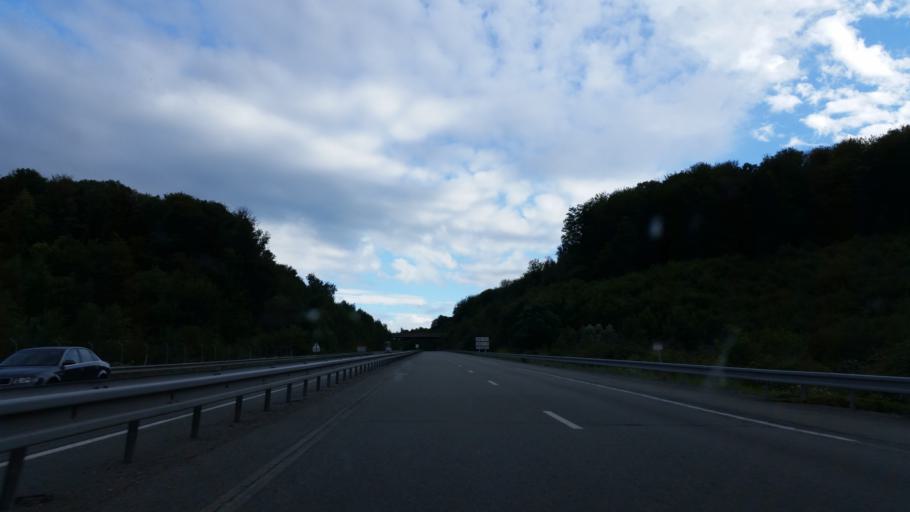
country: FR
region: Franche-Comte
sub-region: Departement de la Haute-Saone
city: Fougerolles
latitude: 47.8593
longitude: 6.3818
